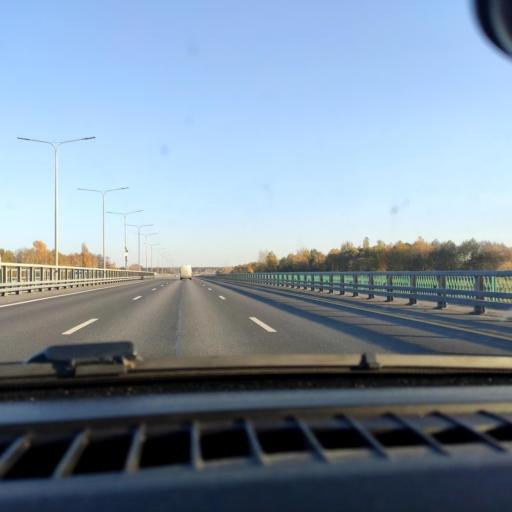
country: RU
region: Voronezj
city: Somovo
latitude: 51.7929
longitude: 39.2677
